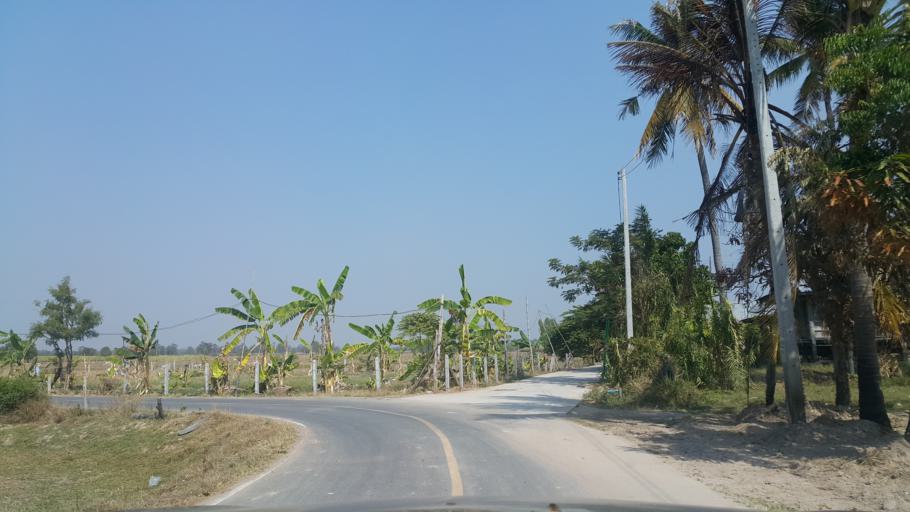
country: TH
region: Buriram
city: Krasang
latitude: 15.0892
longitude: 103.3879
